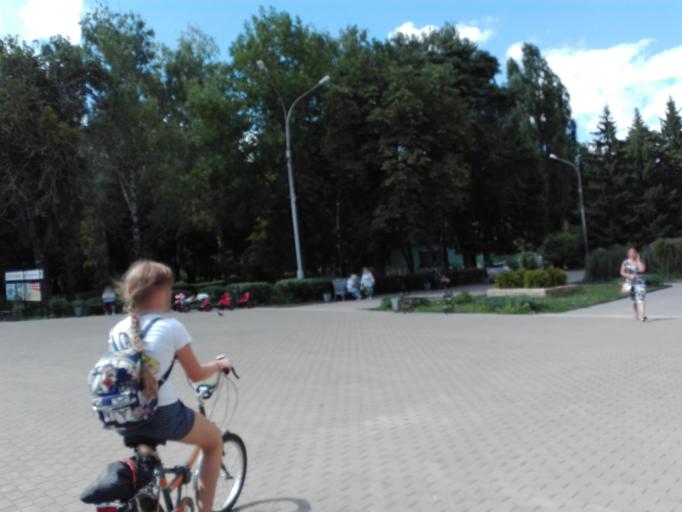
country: RU
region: Lipetsk
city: Lipetsk
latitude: 52.6184
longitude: 39.5924
